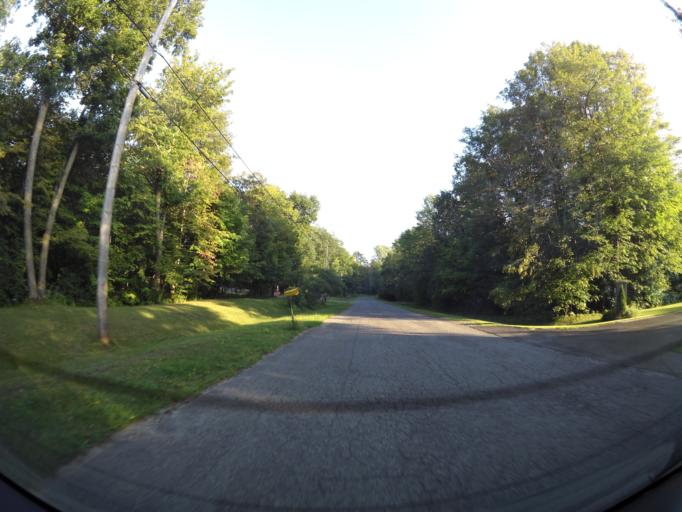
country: CA
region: Ontario
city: Clarence-Rockland
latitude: 45.5018
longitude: -75.4164
